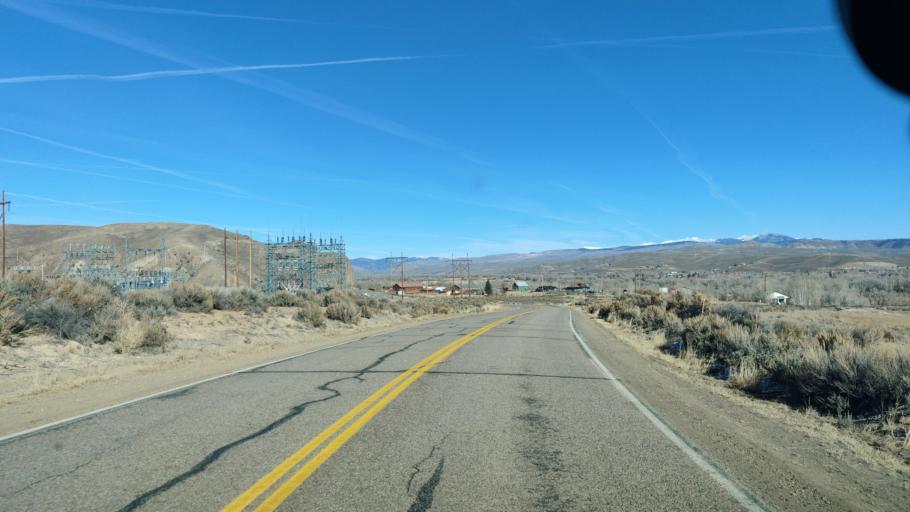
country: US
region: Colorado
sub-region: Gunnison County
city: Gunnison
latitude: 38.5462
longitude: -106.9547
